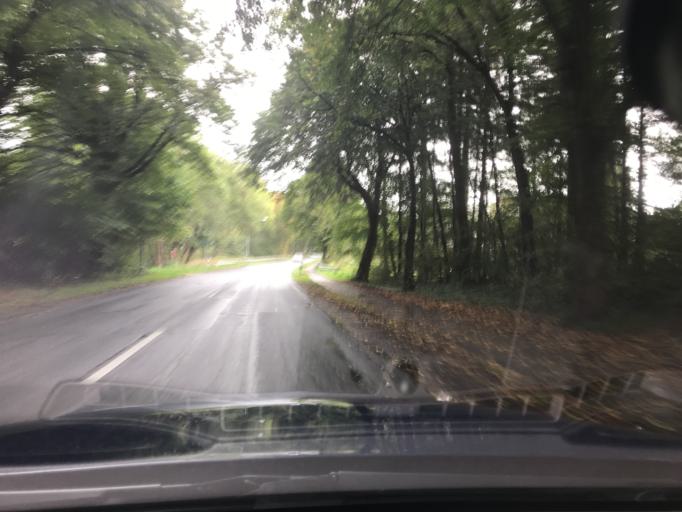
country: DE
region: Lower Saxony
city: Stade
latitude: 53.5773
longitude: 9.4704
